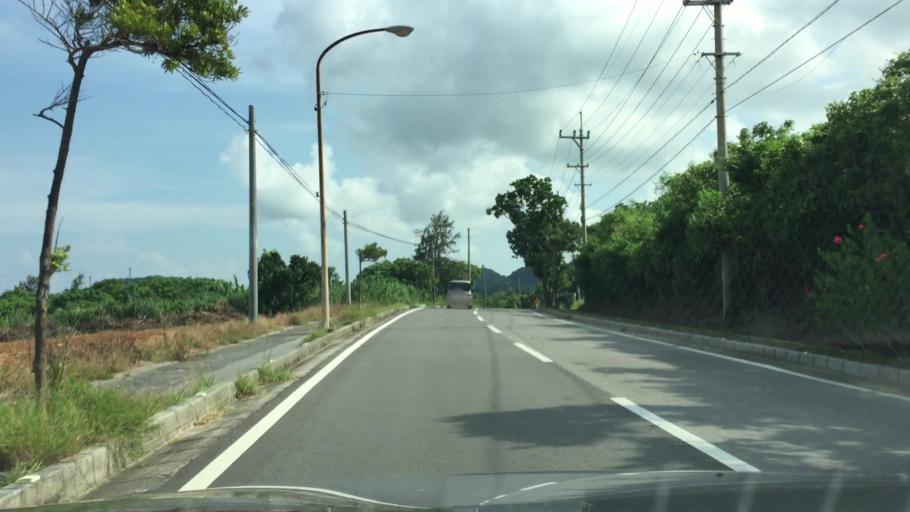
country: JP
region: Okinawa
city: Ishigaki
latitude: 24.4610
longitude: 124.2501
